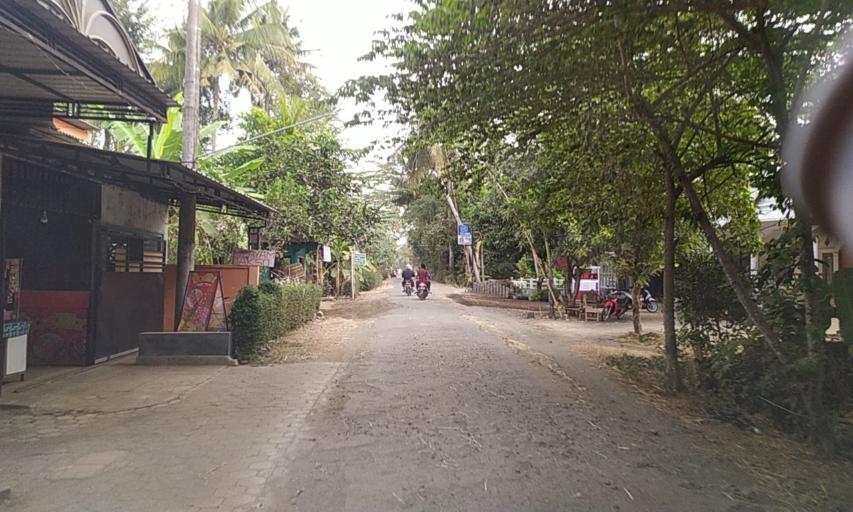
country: ID
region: Central Java
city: Kroya
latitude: -7.6836
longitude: 109.2819
